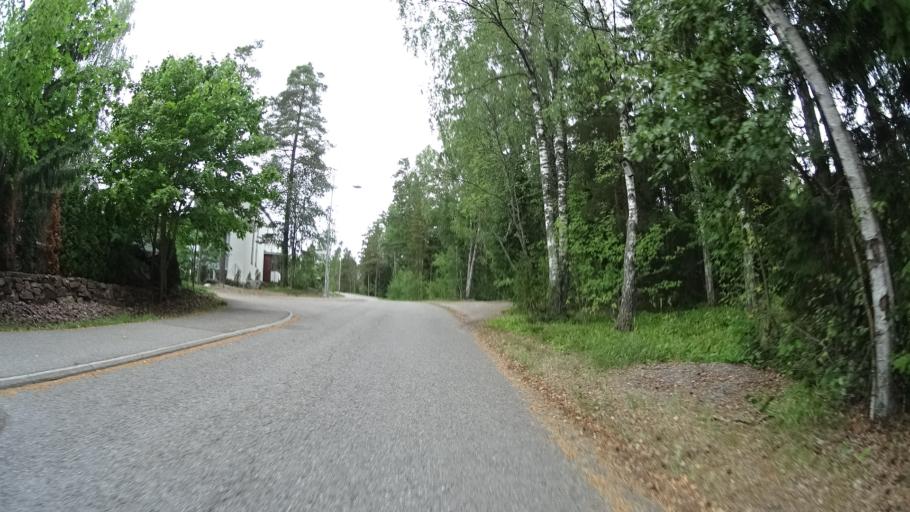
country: FI
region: Uusimaa
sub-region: Helsinki
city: Espoo
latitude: 60.1329
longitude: 24.6717
